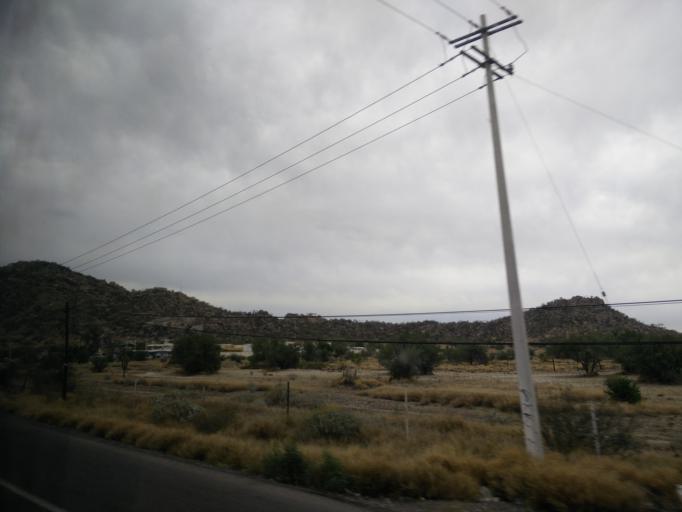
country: MX
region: Sonora
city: Hermosillo
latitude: 29.0118
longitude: -110.9629
